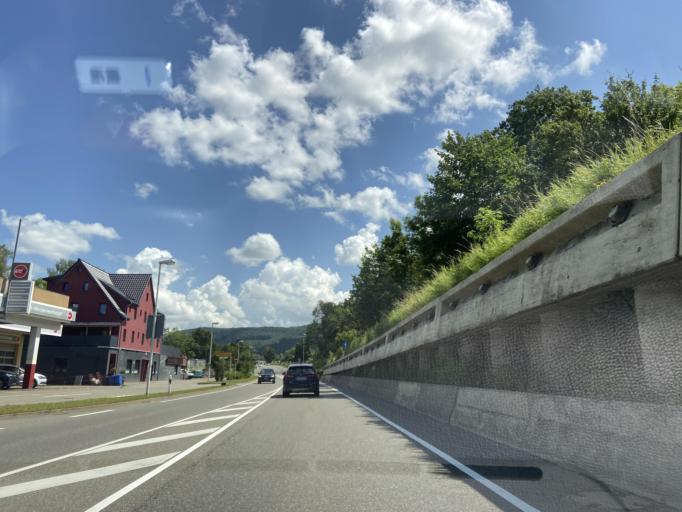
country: DE
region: Baden-Wuerttemberg
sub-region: Tuebingen Region
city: Messstetten
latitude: 48.2199
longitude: 8.9216
